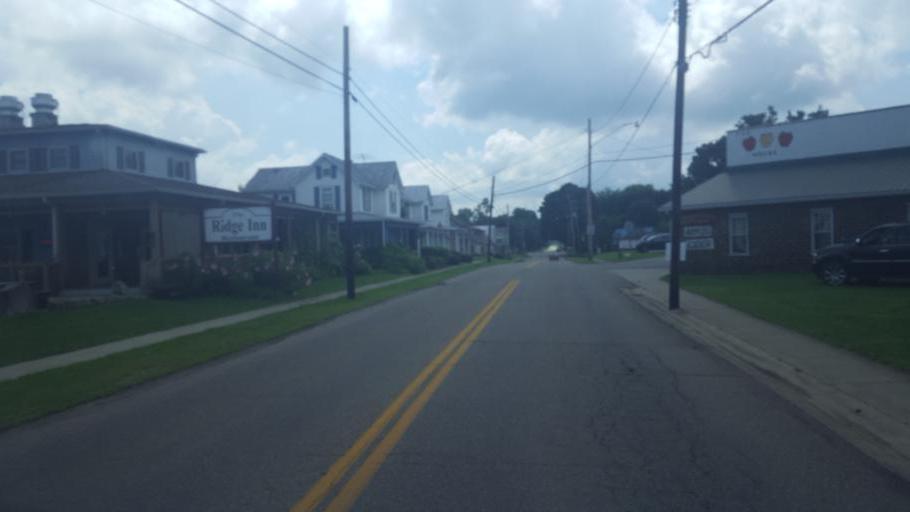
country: US
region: Ohio
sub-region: Ross County
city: Kingston
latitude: 39.4707
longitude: -82.7372
